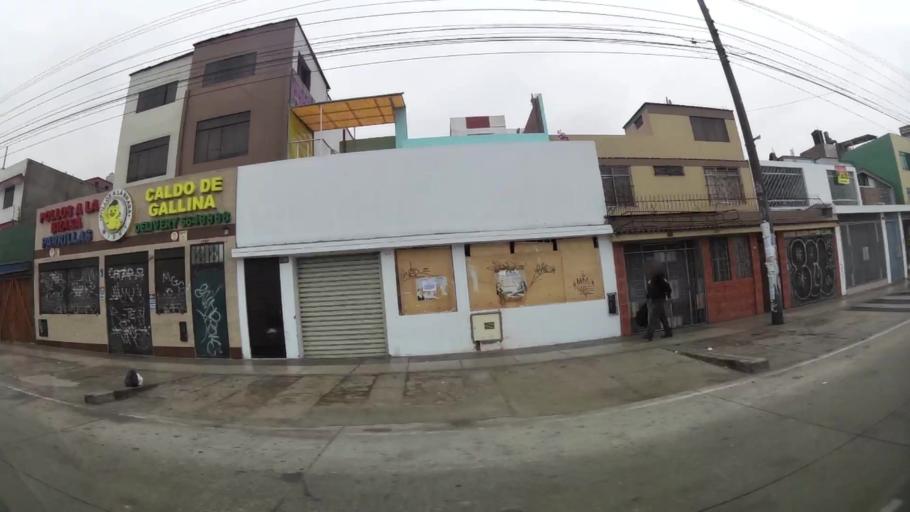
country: PE
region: Callao
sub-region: Callao
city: Callao
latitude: -12.0673
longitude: -77.0778
